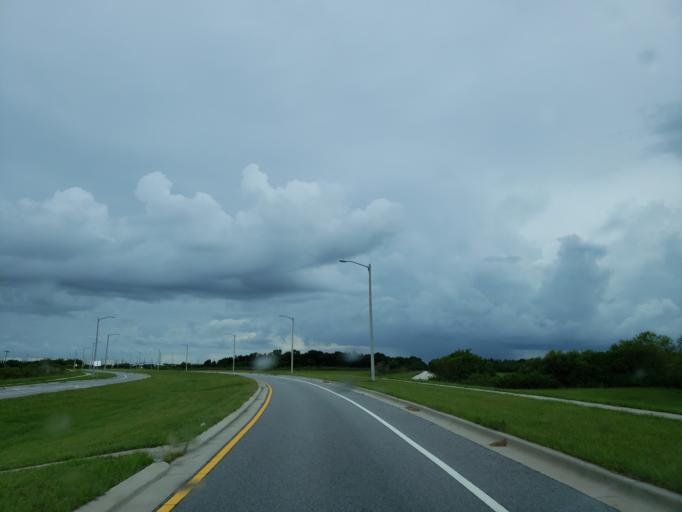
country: US
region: Florida
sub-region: Hillsborough County
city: Ruskin
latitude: 27.7336
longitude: -82.3938
